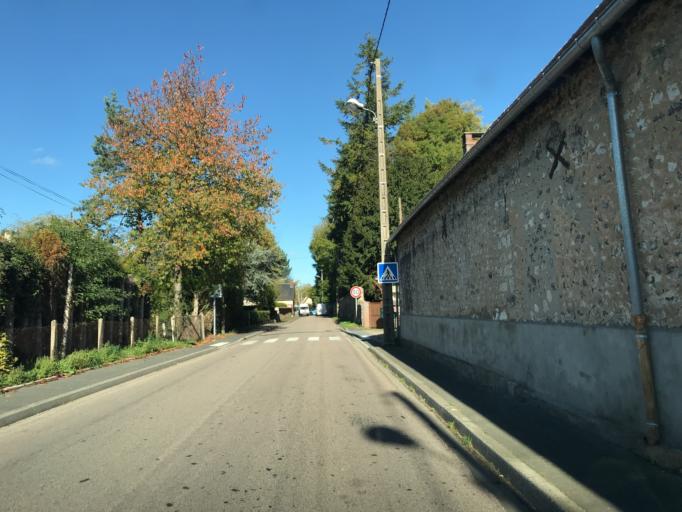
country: FR
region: Haute-Normandie
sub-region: Departement de l'Eure
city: Saint-Aubin-sur-Gaillon
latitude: 49.0915
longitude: 1.2730
